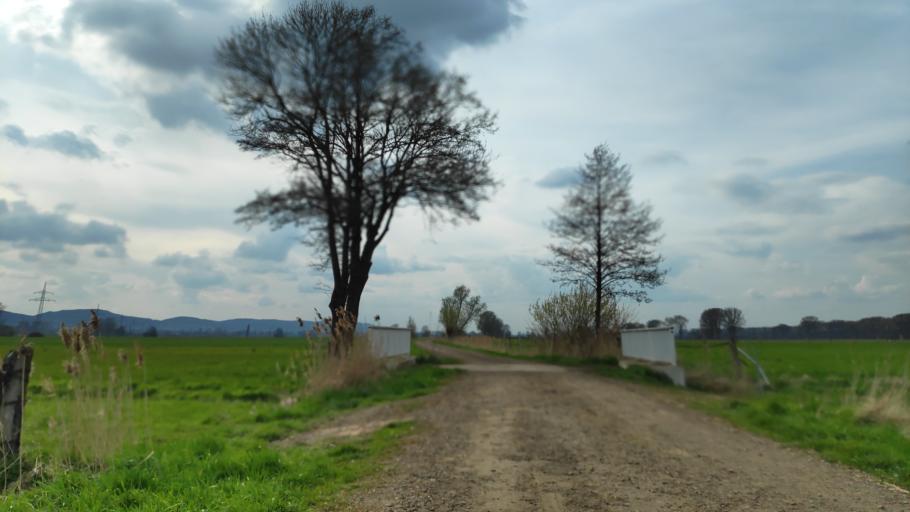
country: DE
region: North Rhine-Westphalia
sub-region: Regierungsbezirk Detmold
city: Minden
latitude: 52.2870
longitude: 8.8607
